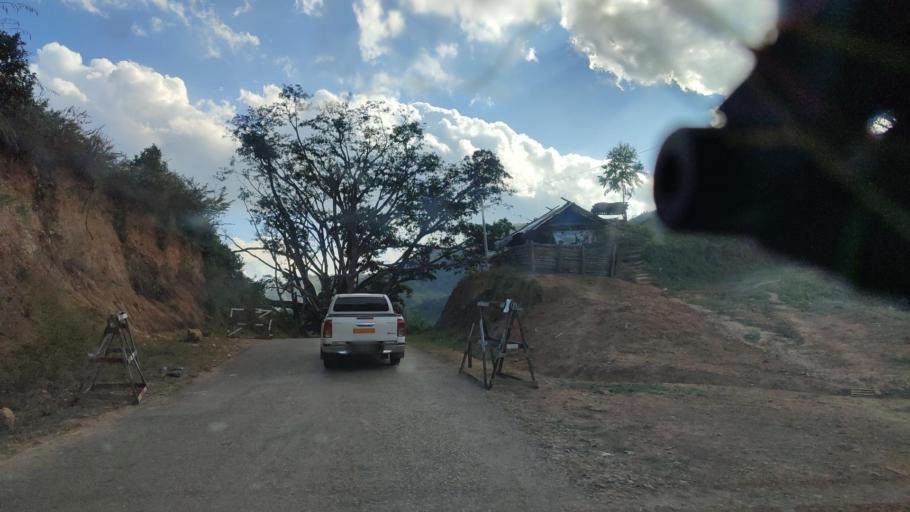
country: MM
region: Shan
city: Taunggyi
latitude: 21.4680
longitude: 97.5966
